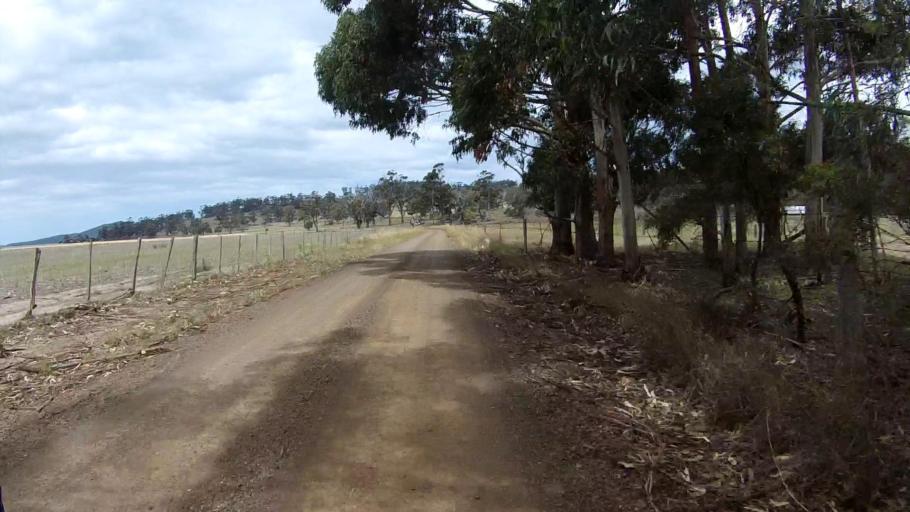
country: AU
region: Tasmania
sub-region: Sorell
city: Sorell
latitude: -42.6578
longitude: 147.9404
